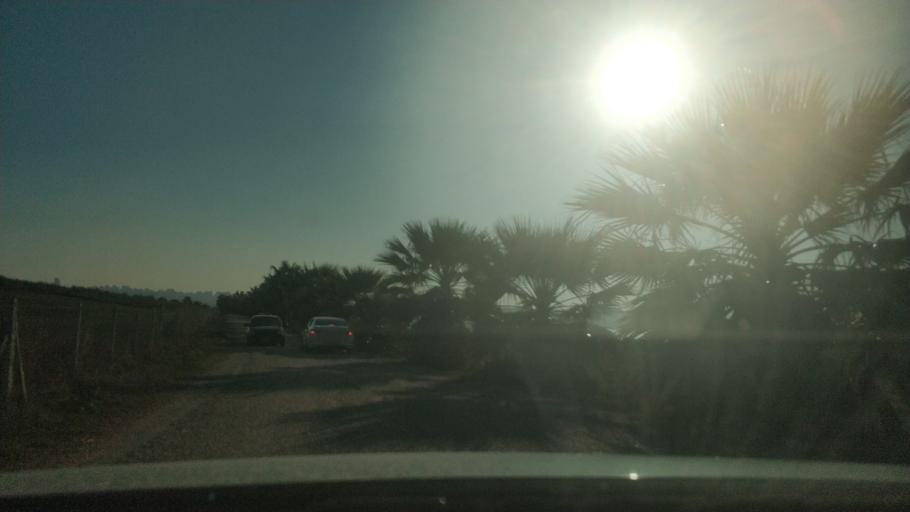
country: TR
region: Adana
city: Adana
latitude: 37.0930
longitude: 35.3016
